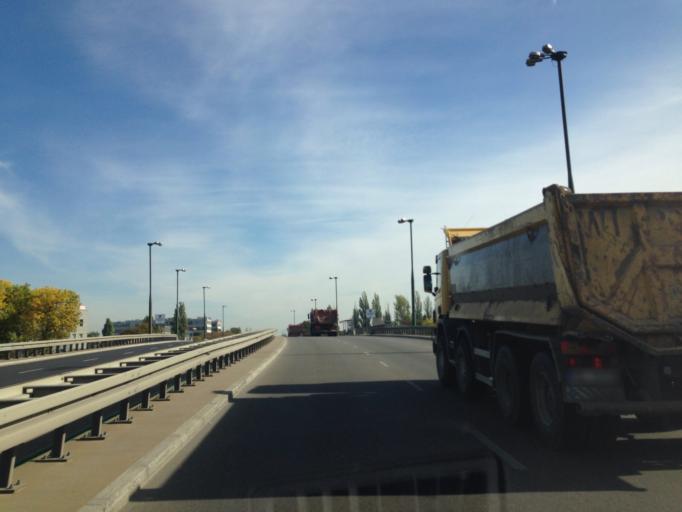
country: PL
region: Masovian Voivodeship
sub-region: Warszawa
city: Wlochy
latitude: 52.1947
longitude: 20.9340
